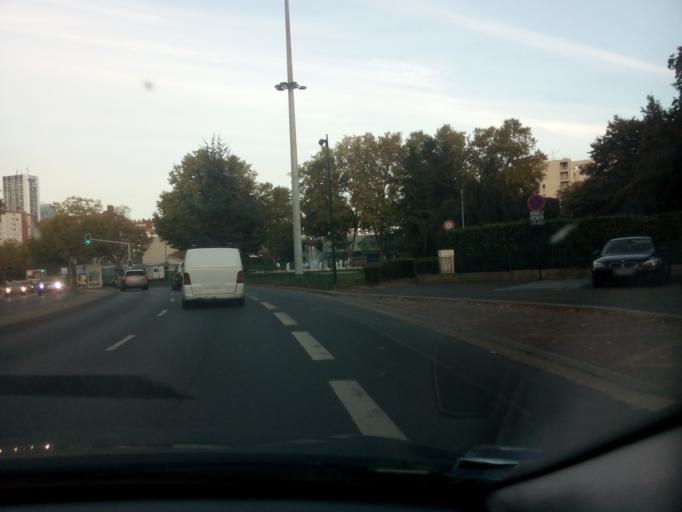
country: FR
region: Ile-de-France
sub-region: Departement des Hauts-de-Seine
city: Puteaux
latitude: 48.8853
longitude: 2.2262
